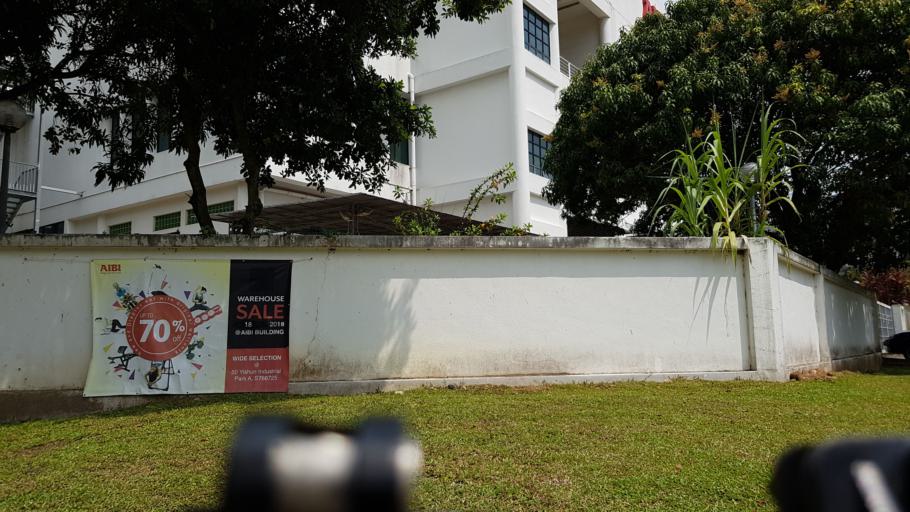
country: MY
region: Johor
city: Kampung Pasir Gudang Baru
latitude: 1.4407
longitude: 103.8344
